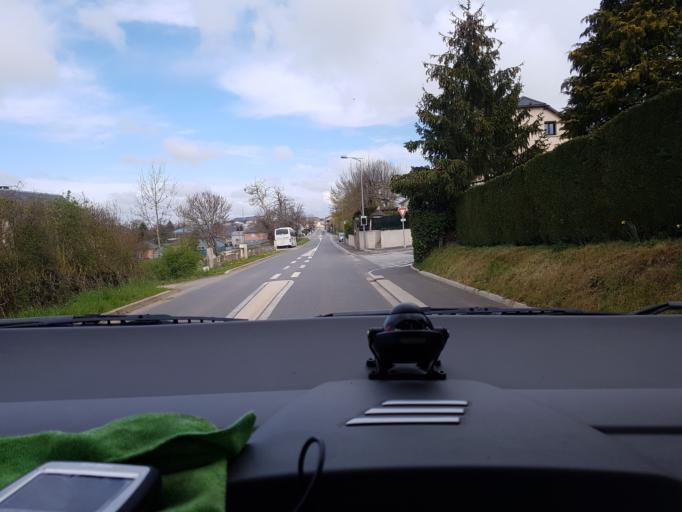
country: FR
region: Midi-Pyrenees
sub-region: Departement de l'Aveyron
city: Colombies
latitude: 44.4035
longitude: 2.2941
